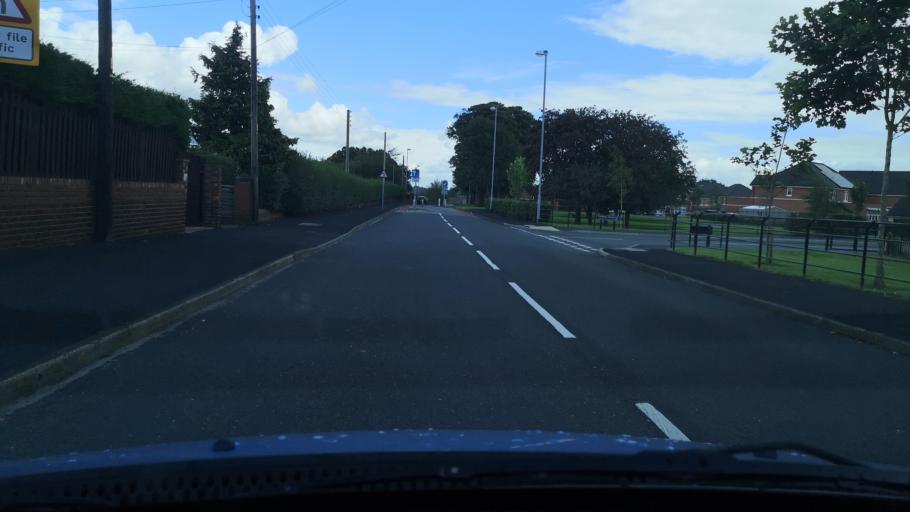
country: GB
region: England
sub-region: City and Borough of Wakefield
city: Crigglestone
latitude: 53.6431
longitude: -1.5185
